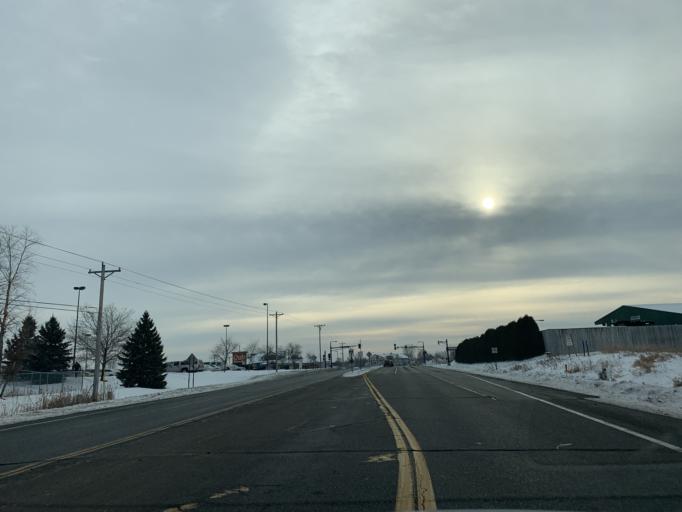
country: US
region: Minnesota
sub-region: Washington County
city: Forest Lake
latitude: 45.2828
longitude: -93.0121
